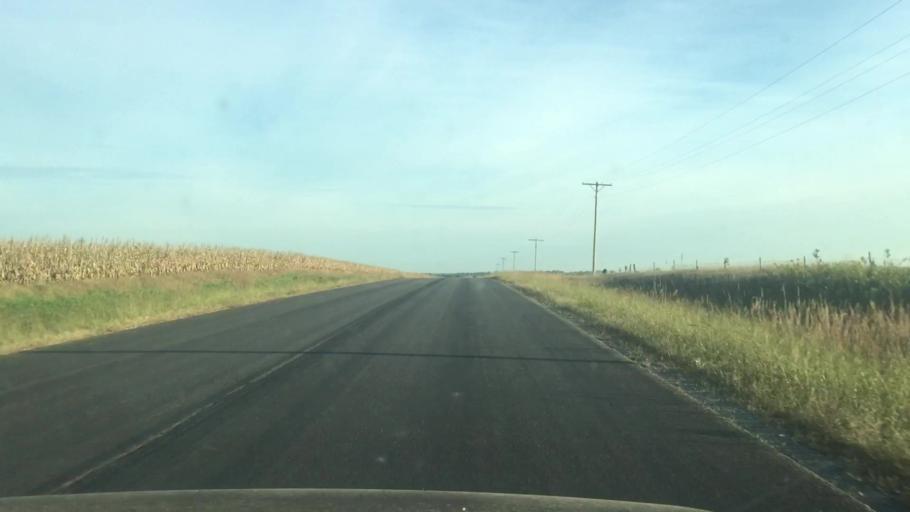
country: US
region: Kansas
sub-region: Marshall County
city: Marysville
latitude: 39.9186
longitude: -96.6009
